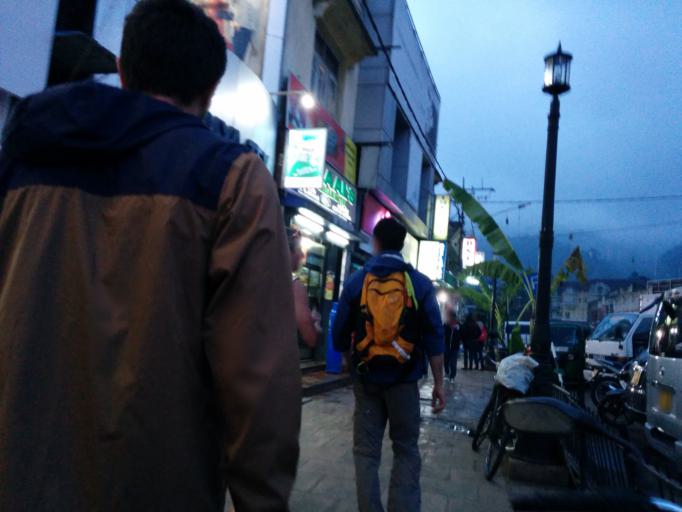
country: LK
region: Central
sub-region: Nuwara Eliya District
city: Nuwara Eliya
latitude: 6.9724
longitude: 80.7667
